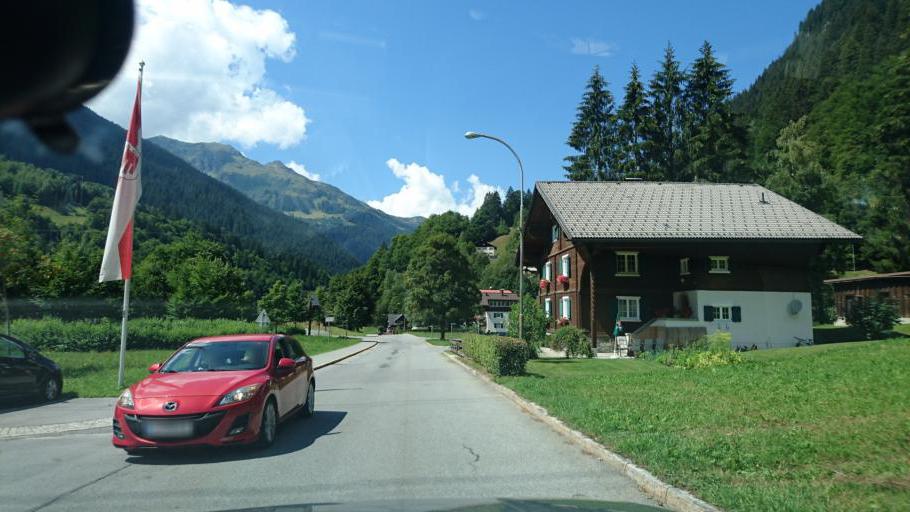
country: AT
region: Vorarlberg
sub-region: Politischer Bezirk Bludenz
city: Gaschurn
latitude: 46.9701
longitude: 10.0578
